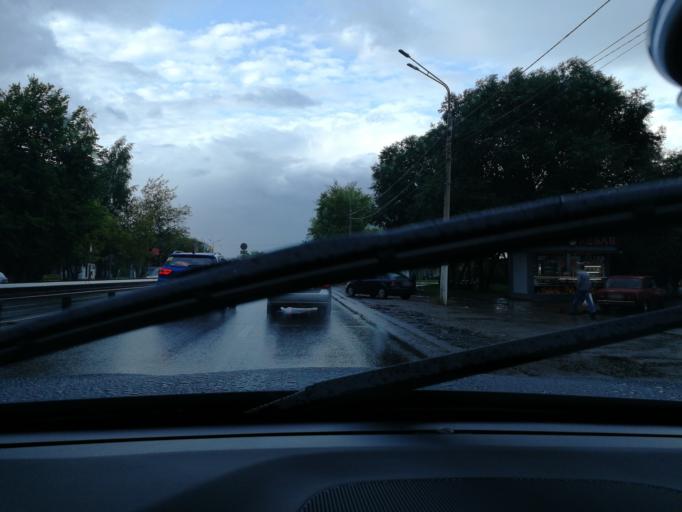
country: RU
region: Moskovskaya
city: Shcherbinka
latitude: 55.4796
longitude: 37.5650
